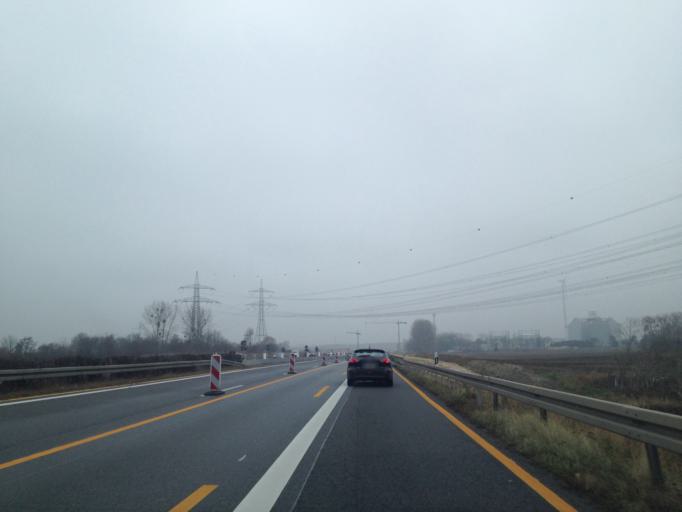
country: DE
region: Berlin
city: Blankenfelde
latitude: 52.6545
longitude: 13.4148
